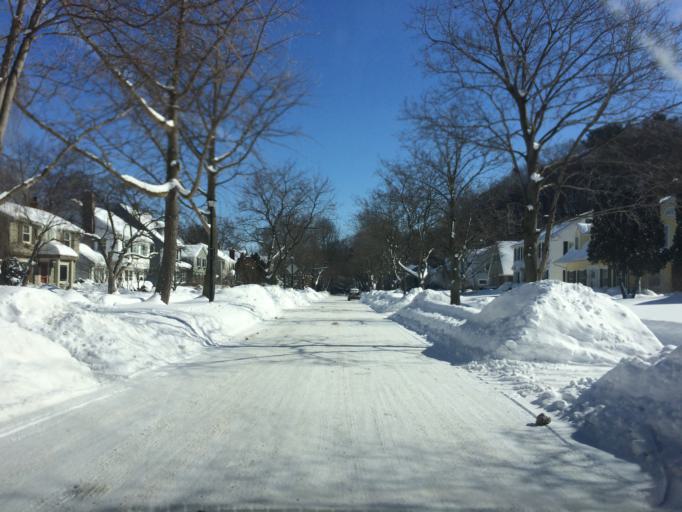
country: US
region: New York
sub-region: Monroe County
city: Rochester
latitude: 43.1343
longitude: -77.6022
